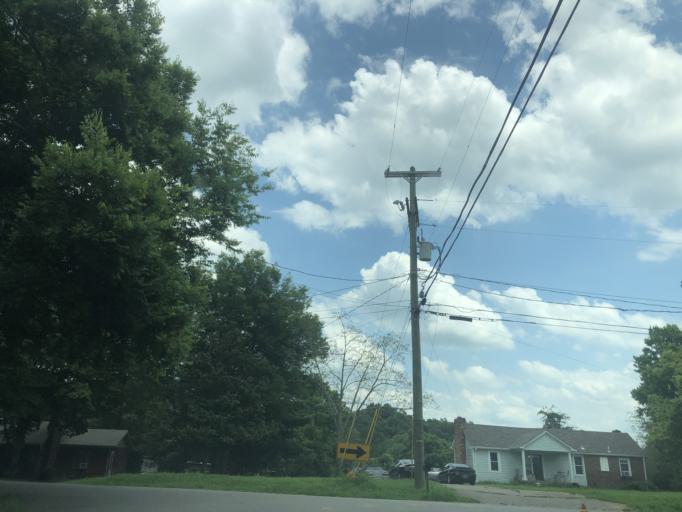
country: US
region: Tennessee
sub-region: Williamson County
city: Brentwood Estates
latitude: 36.0233
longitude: -86.7304
